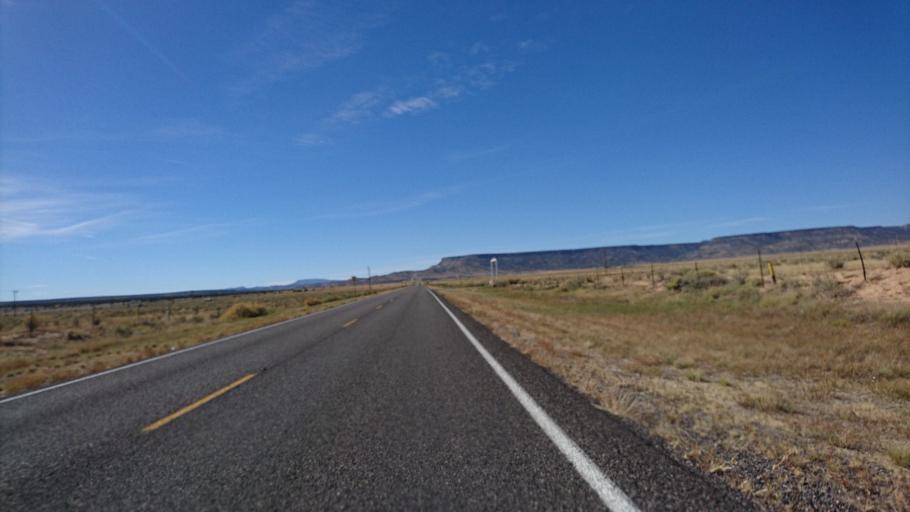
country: US
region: New Mexico
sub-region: Cibola County
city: Skyline-Ganipa
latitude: 35.0825
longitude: -107.6077
